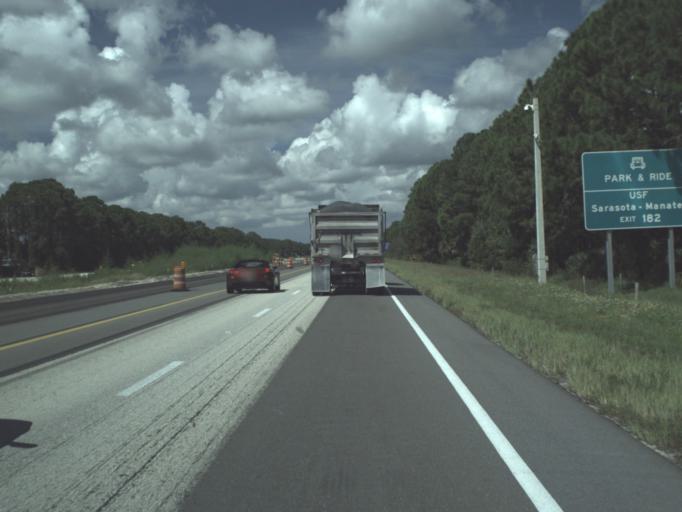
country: US
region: Florida
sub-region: Sarasota County
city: North Port
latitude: 27.0993
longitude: -82.1823
